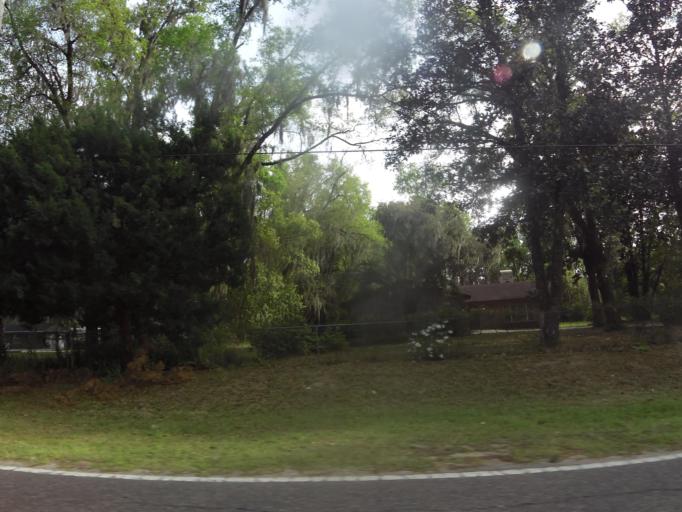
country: US
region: Florida
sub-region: Duval County
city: Jacksonville
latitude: 30.2985
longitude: -81.7607
